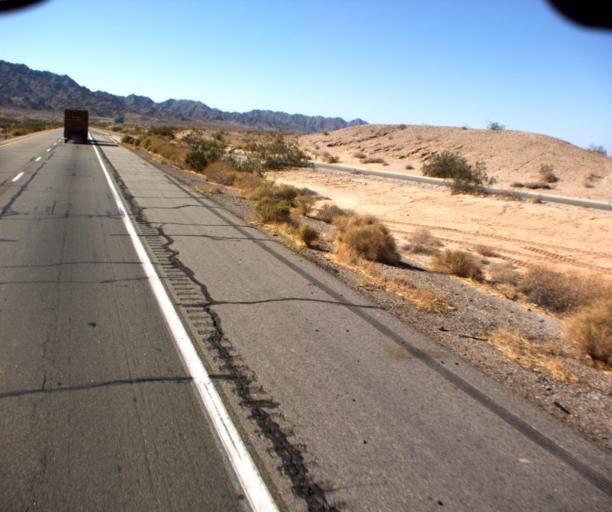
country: US
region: Arizona
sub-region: Yuma County
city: Fortuna Foothills
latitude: 32.6671
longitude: -114.2832
